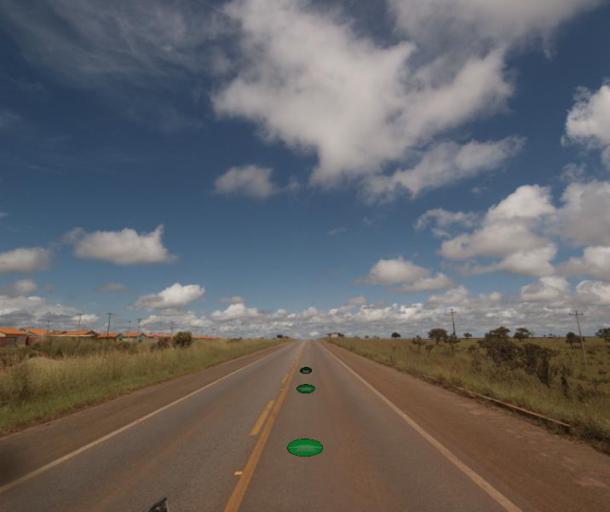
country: BR
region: Federal District
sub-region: Brasilia
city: Brasilia
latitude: -15.7452
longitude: -48.4109
